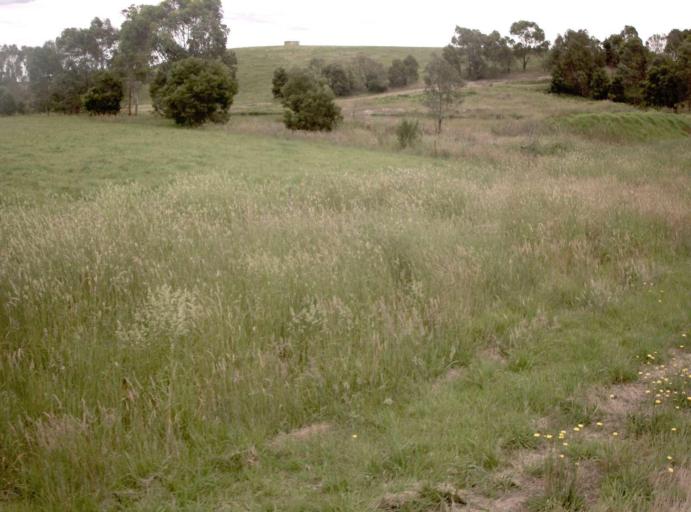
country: AU
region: Victoria
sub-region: East Gippsland
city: Bairnsdale
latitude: -37.7712
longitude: 147.3243
